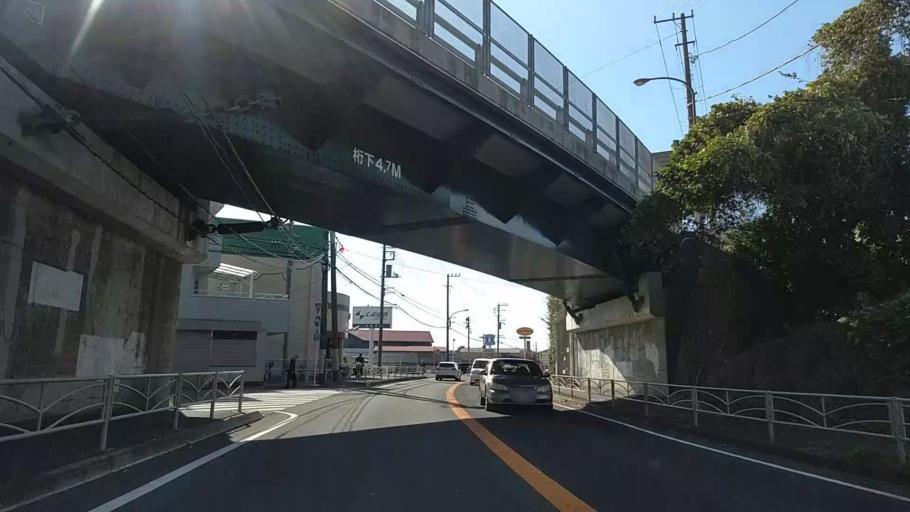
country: JP
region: Kanagawa
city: Hiratsuka
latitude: 35.3164
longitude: 139.3227
